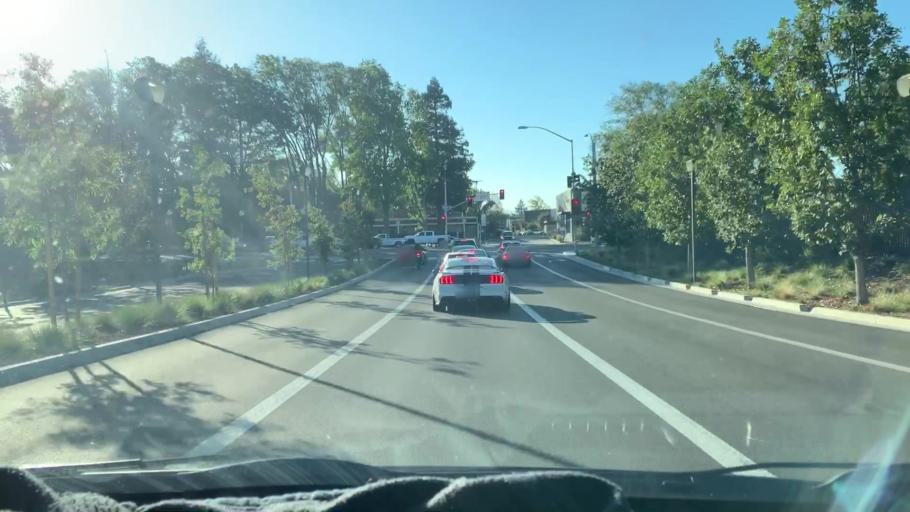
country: US
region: California
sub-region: Santa Clara County
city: Cupertino
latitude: 37.3350
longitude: -122.0134
